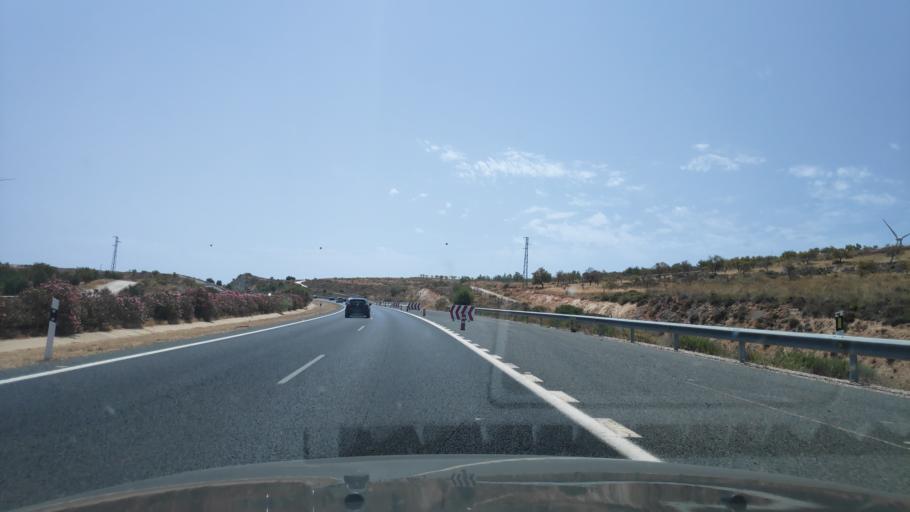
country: ES
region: Andalusia
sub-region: Provincia de Granada
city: Padul
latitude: 37.0075
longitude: -3.6393
